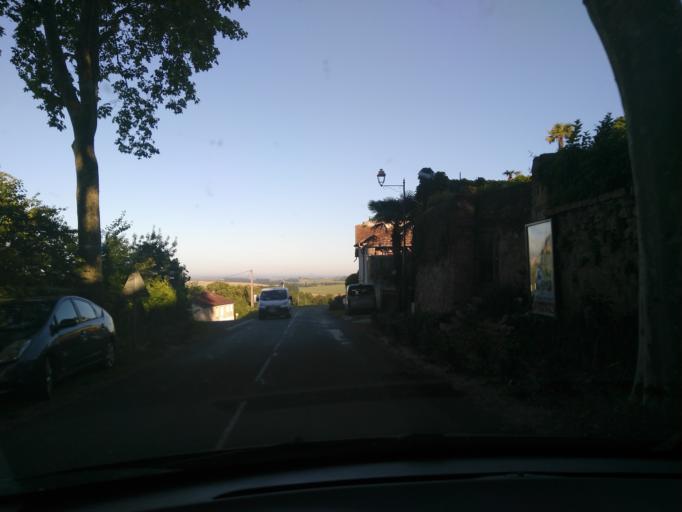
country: FR
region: Midi-Pyrenees
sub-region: Departement du Gers
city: Valence-sur-Baise
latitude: 43.8756
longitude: 0.4610
